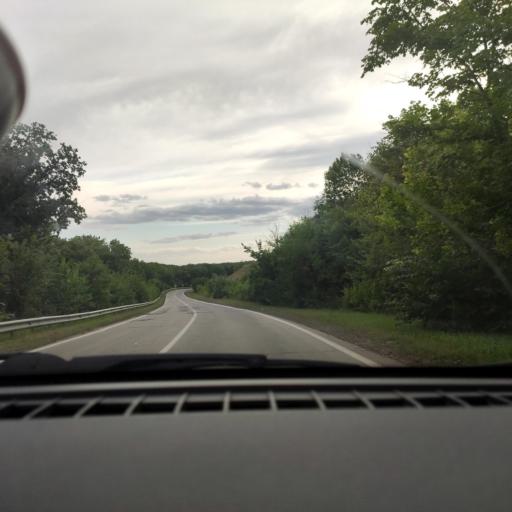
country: RU
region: Samara
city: Krasnyy Yar
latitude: 53.4396
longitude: 50.5890
